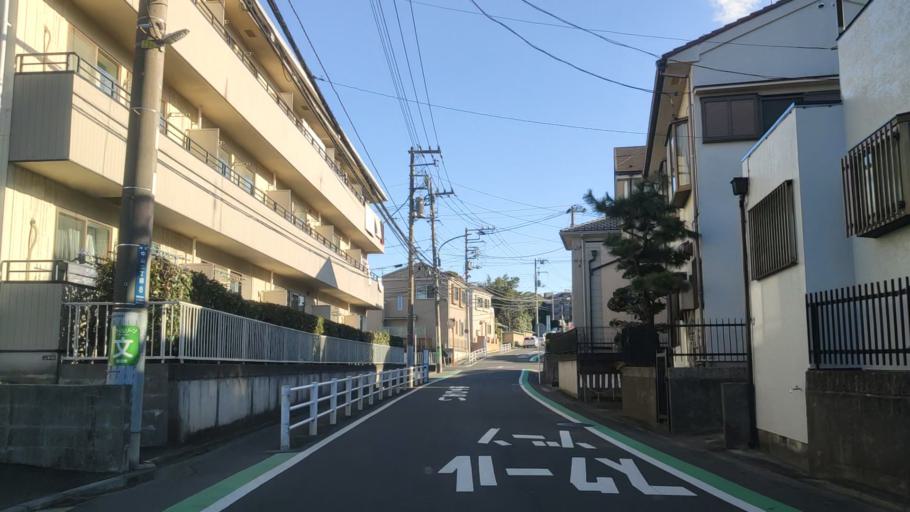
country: JP
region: Tokyo
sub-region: Machida-shi
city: Machida
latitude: 35.5144
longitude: 139.5475
